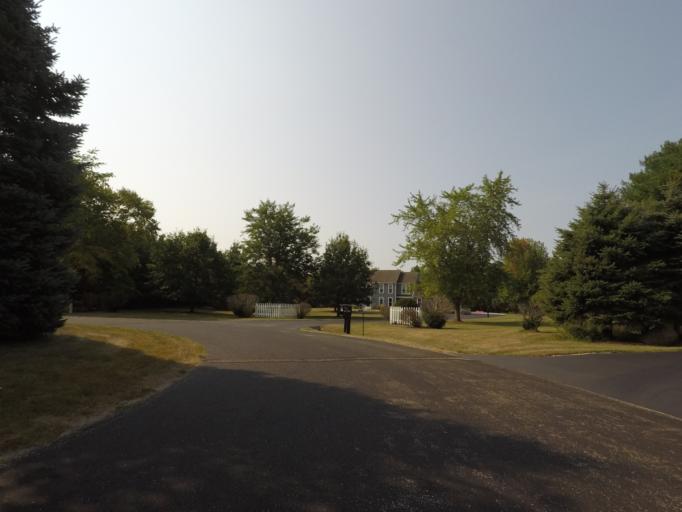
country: US
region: Wisconsin
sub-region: Waukesha County
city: Delafield
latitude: 43.0269
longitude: -88.4283
